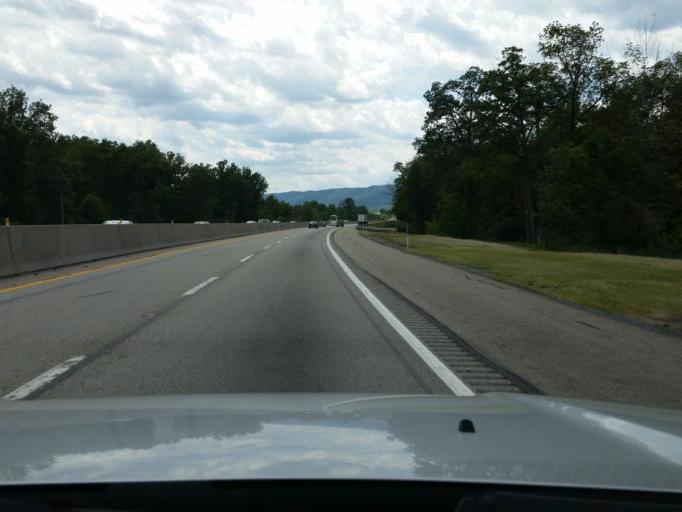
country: US
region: Pennsylvania
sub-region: Franklin County
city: Doylestown
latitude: 40.1275
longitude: -77.7480
